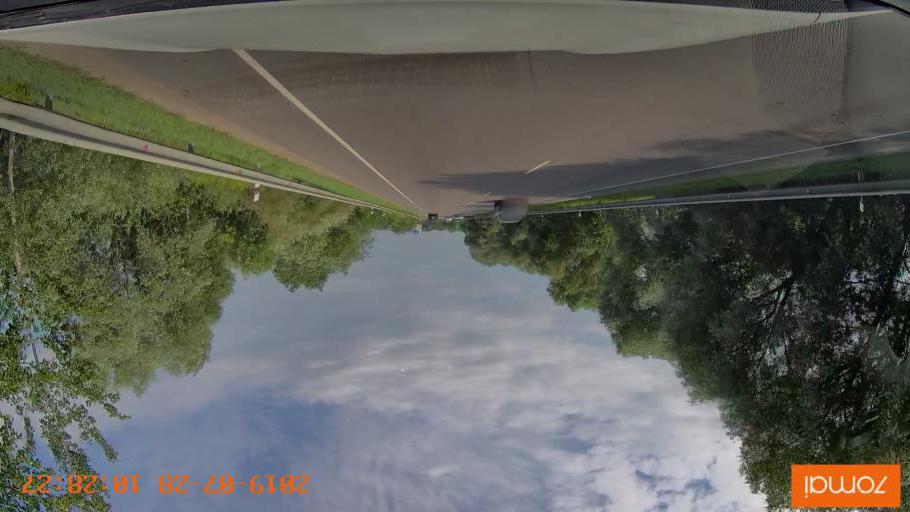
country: RU
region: Kaliningrad
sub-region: Gorod Kaliningrad
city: Kaliningrad
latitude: 54.7689
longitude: 20.4988
